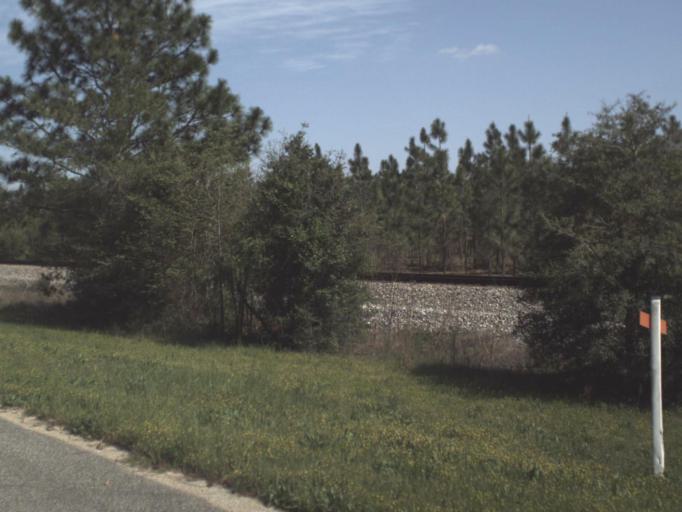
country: US
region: Florida
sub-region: Okaloosa County
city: Crestview
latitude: 30.7512
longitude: -86.4469
